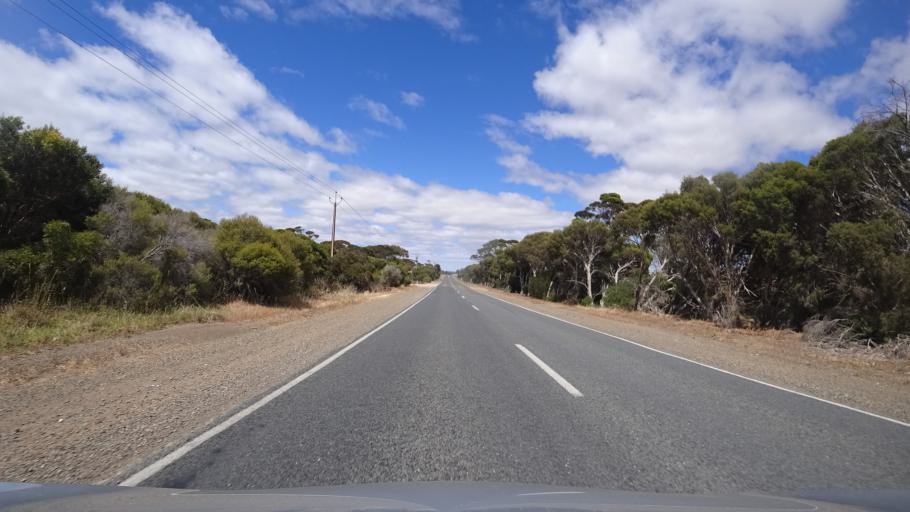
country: AU
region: South Australia
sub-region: Kangaroo Island
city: Kingscote
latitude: -35.6646
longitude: 137.5980
